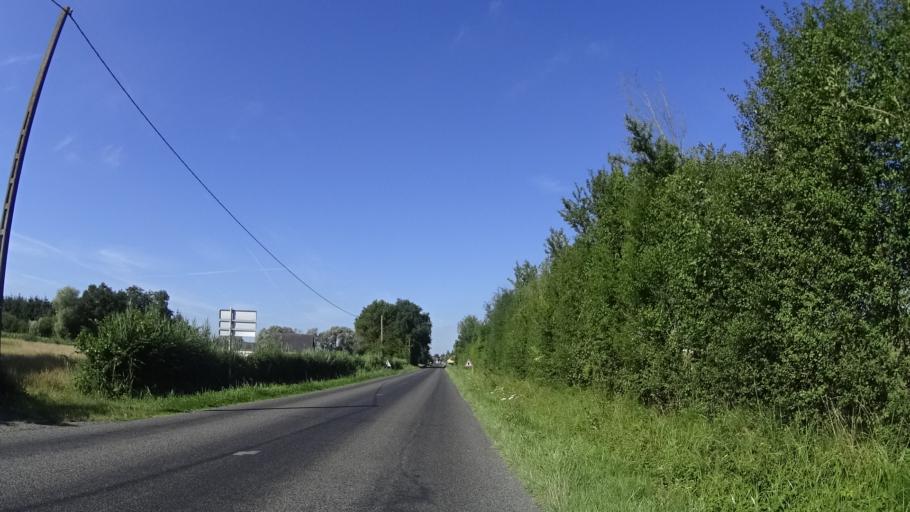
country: FR
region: Pays de la Loire
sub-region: Departement de Maine-et-Loire
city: Tierce
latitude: 47.6256
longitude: -0.4530
